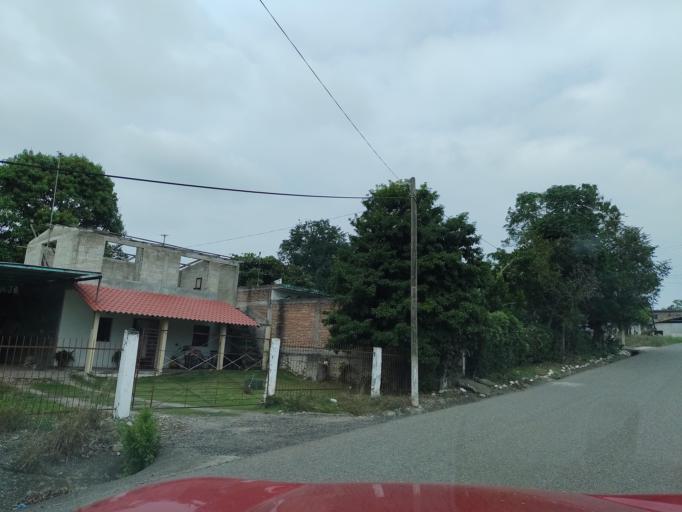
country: MX
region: Veracruz
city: Agua Dulce
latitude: 20.3412
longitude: -97.2918
